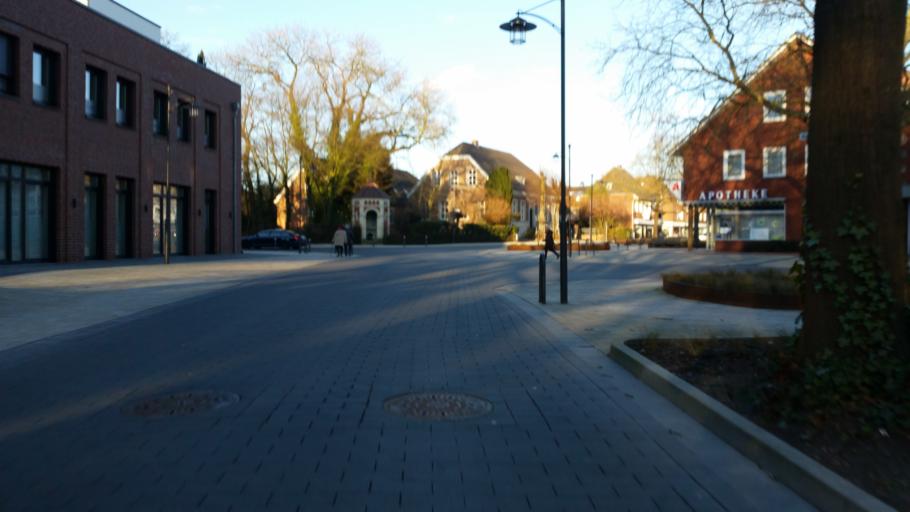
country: DE
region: North Rhine-Westphalia
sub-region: Regierungsbezirk Munster
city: Neuenkirchen
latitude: 52.2431
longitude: 7.3687
